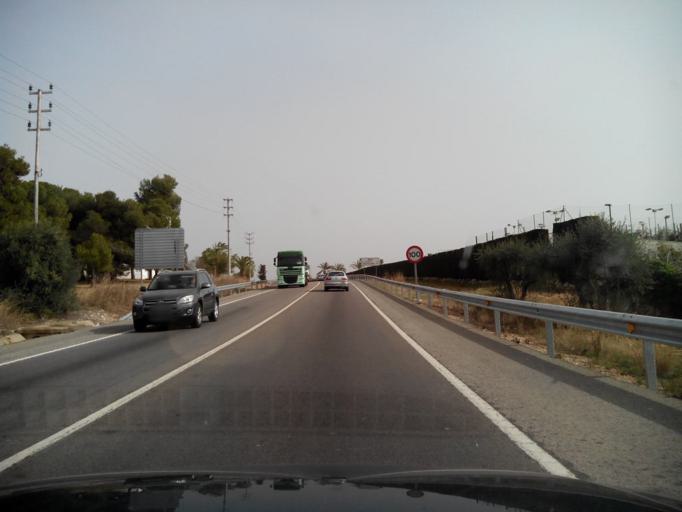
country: ES
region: Catalonia
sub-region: Provincia de Tarragona
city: Roda de Bara
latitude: 41.1688
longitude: 1.4614
